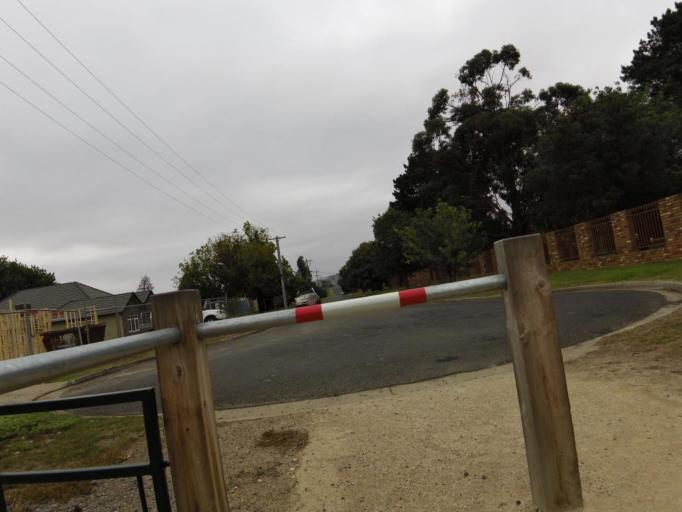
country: AU
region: Victoria
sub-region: Moorabool
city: Bacchus Marsh
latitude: -37.6637
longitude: 144.4486
